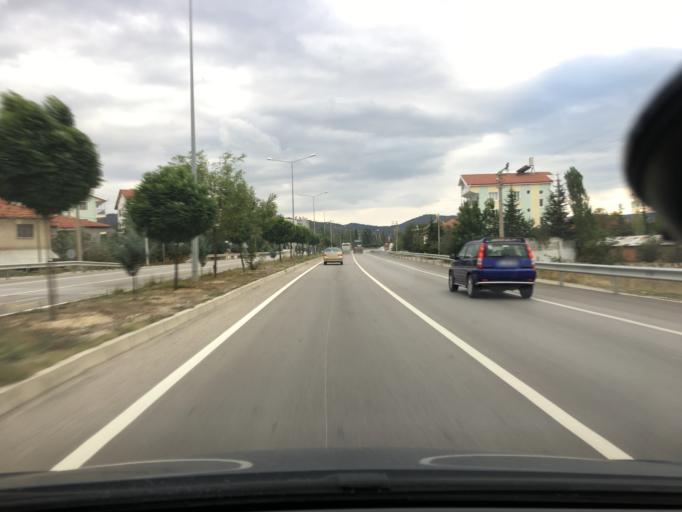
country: TR
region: Afyonkarahisar
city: Sincanli
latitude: 38.7299
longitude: 30.3453
